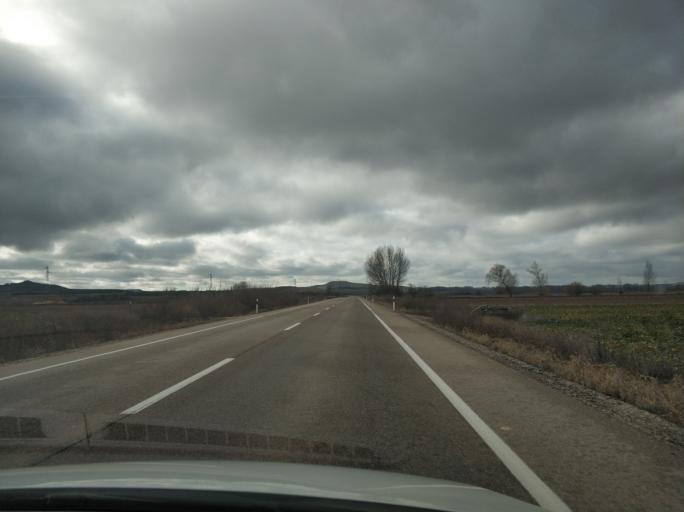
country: ES
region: Castille and Leon
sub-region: Provincia de Soria
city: San Esteban de Gormaz
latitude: 41.5676
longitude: -3.2293
